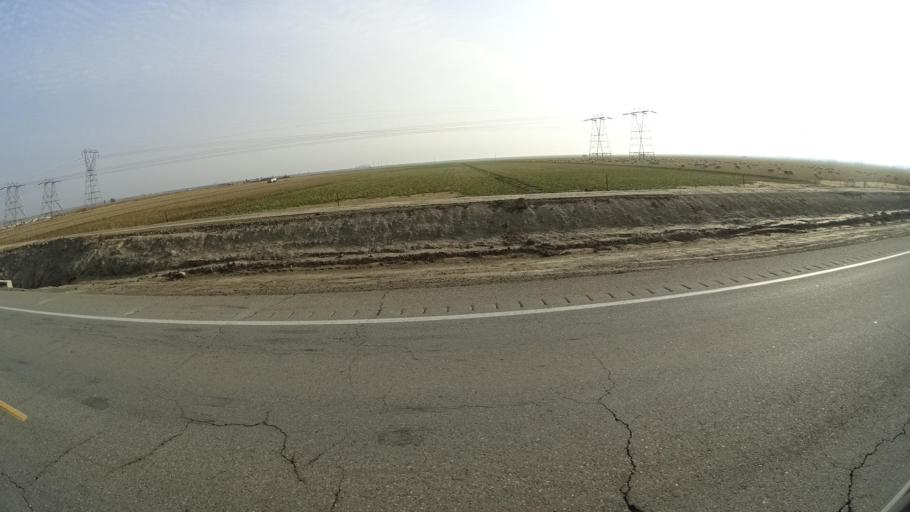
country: US
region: California
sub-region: Kern County
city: Weedpatch
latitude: 35.1749
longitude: -118.9147
